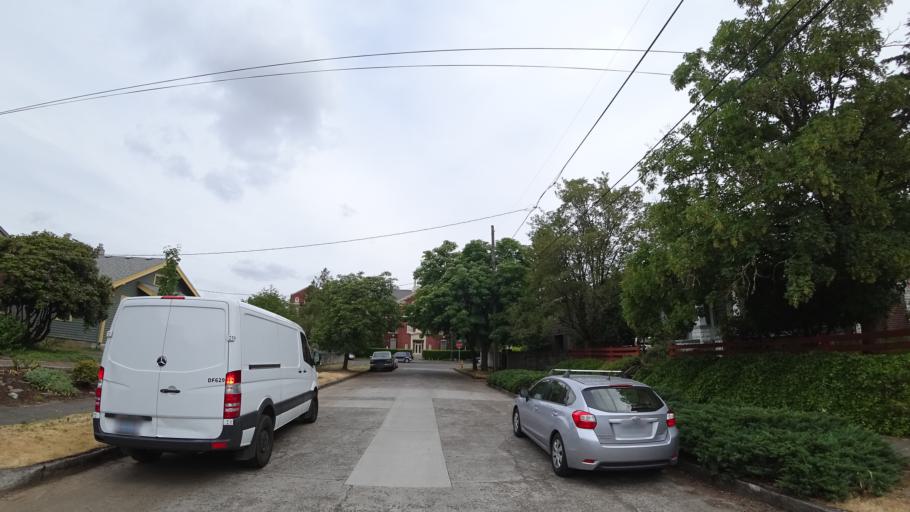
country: US
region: Oregon
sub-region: Multnomah County
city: Portland
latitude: 45.5712
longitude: -122.6728
